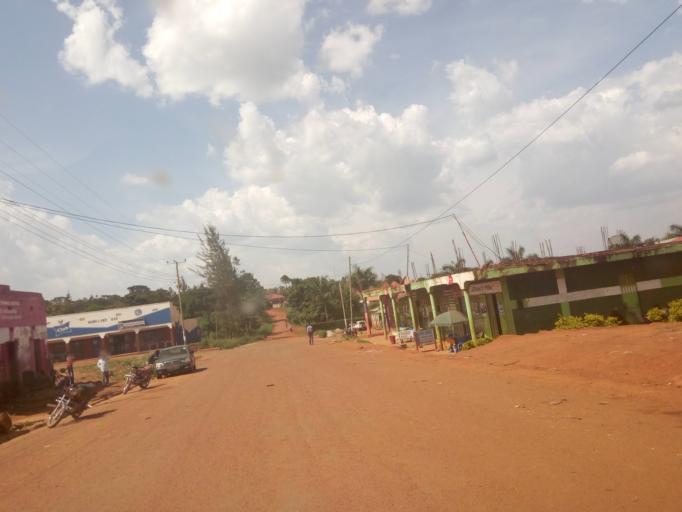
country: UG
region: Western Region
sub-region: Masindi District
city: Masindi
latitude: 1.6837
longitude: 31.7218
